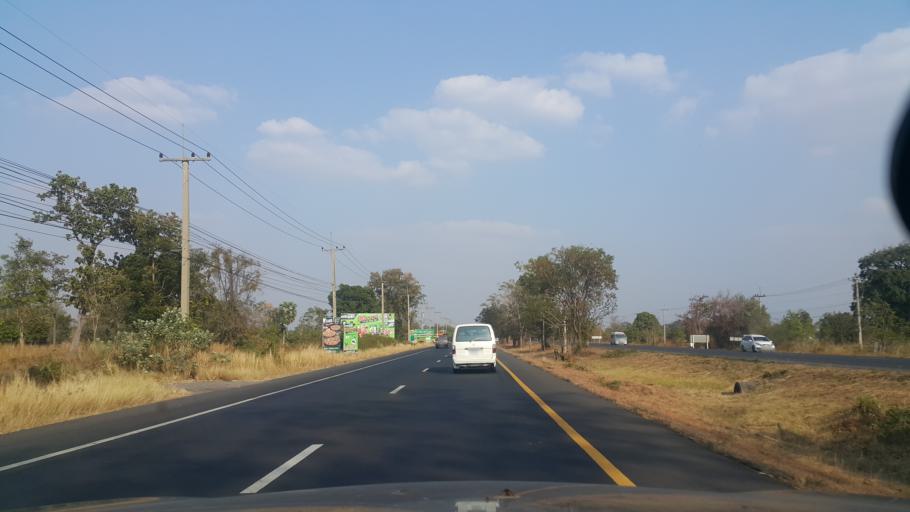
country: TH
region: Buriram
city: Nang Rong
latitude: 14.6360
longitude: 102.7496
